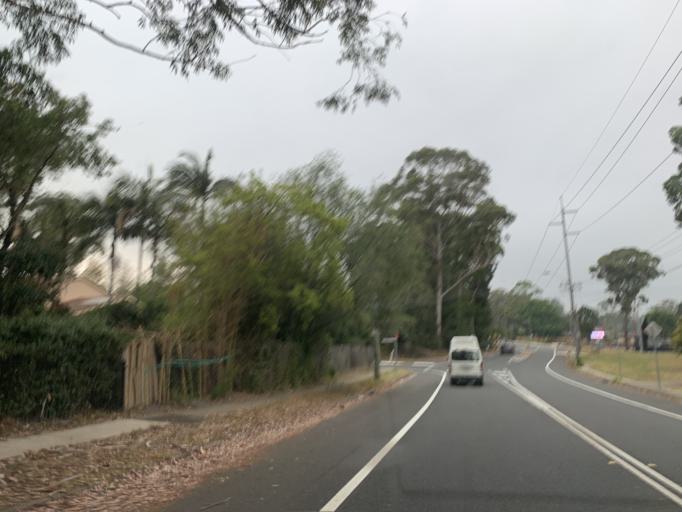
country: AU
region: New South Wales
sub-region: The Hills Shire
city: West Pennant
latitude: -33.7335
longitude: 151.0445
